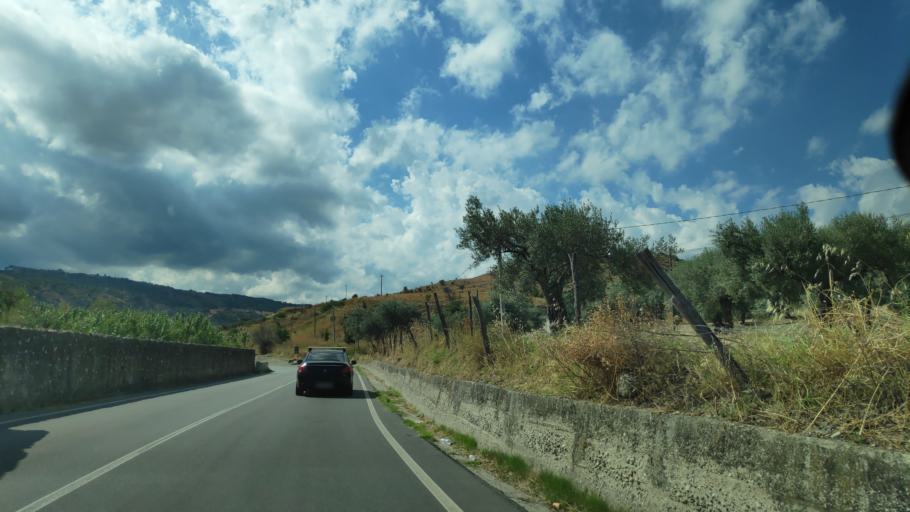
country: IT
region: Calabria
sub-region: Provincia di Catanzaro
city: Santa Caterina dello Ionio Marina
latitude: 38.5271
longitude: 16.5583
